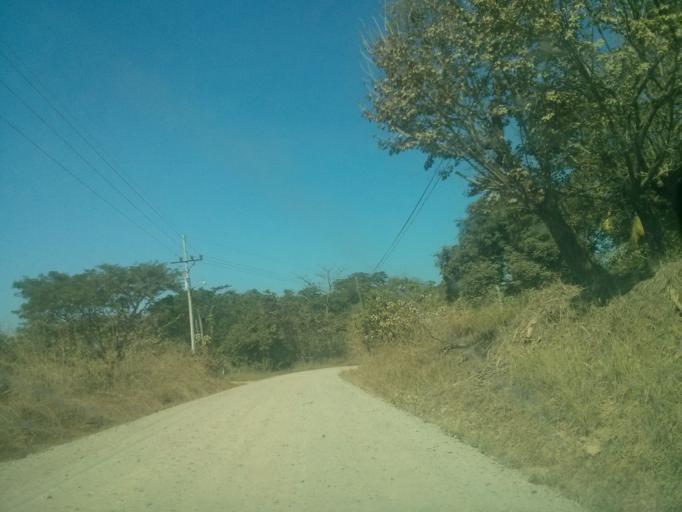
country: CR
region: Puntarenas
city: Paquera
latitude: 9.6737
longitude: -85.1140
